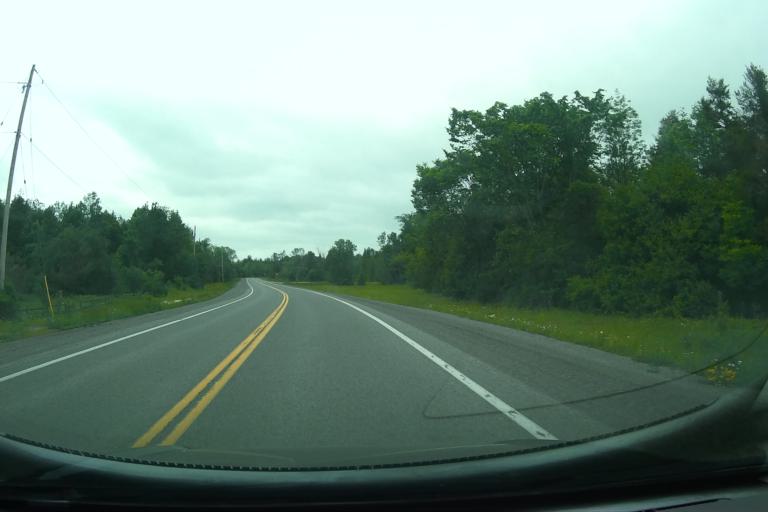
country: CA
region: Ontario
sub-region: Lanark County
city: Smiths Falls
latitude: 45.0162
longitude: -75.8426
